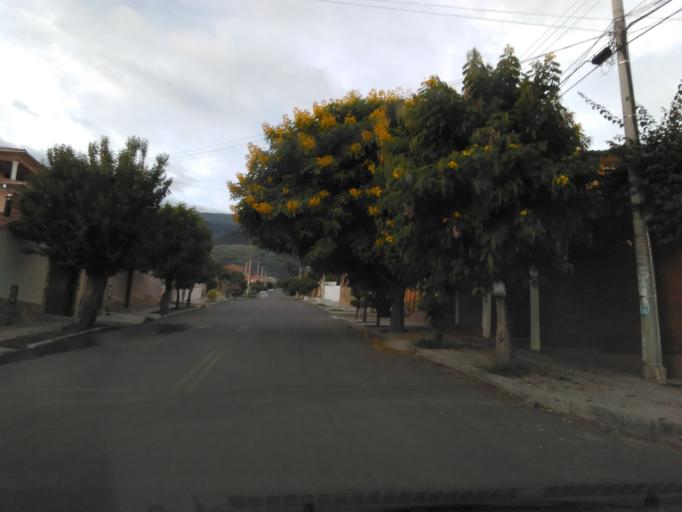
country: BO
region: Cochabamba
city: Cochabamba
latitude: -17.3612
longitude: -66.1562
